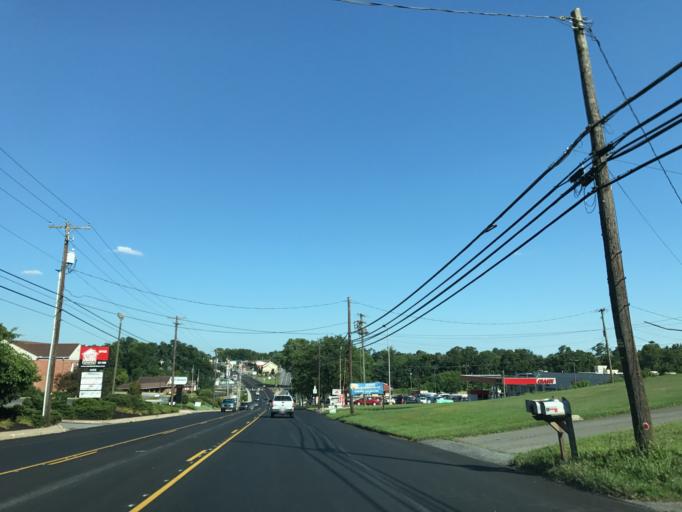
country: US
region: Pennsylvania
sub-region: Lancaster County
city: Elizabethtown
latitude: 40.1409
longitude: -76.5917
